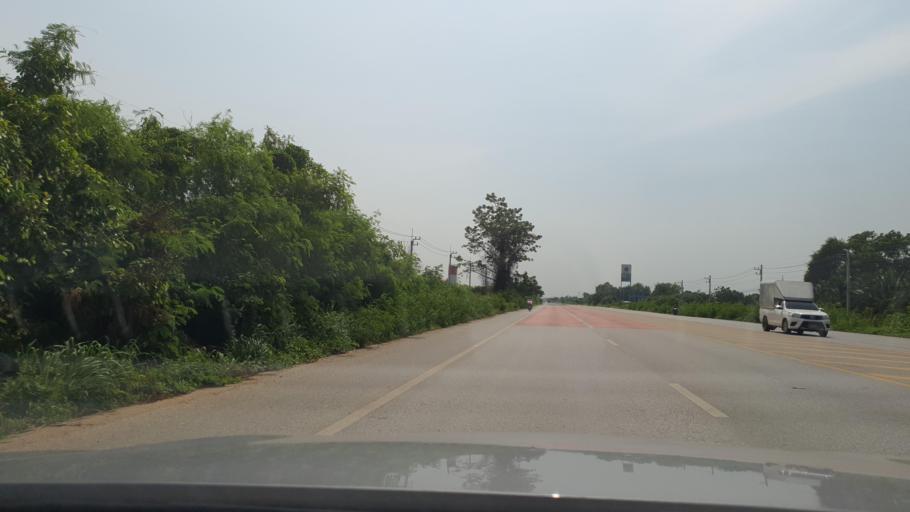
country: TH
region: Phitsanulok
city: Bang Rakam
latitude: 16.7652
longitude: 100.1326
